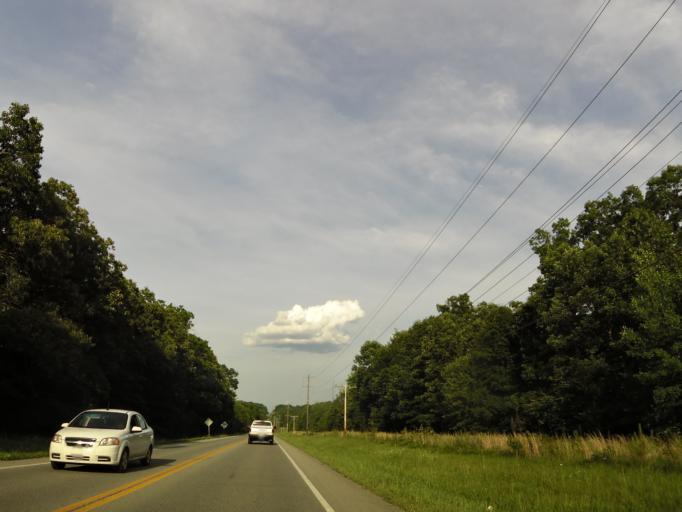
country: US
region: Tennessee
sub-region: Dickson County
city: Dickson
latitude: 36.0896
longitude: -87.4811
